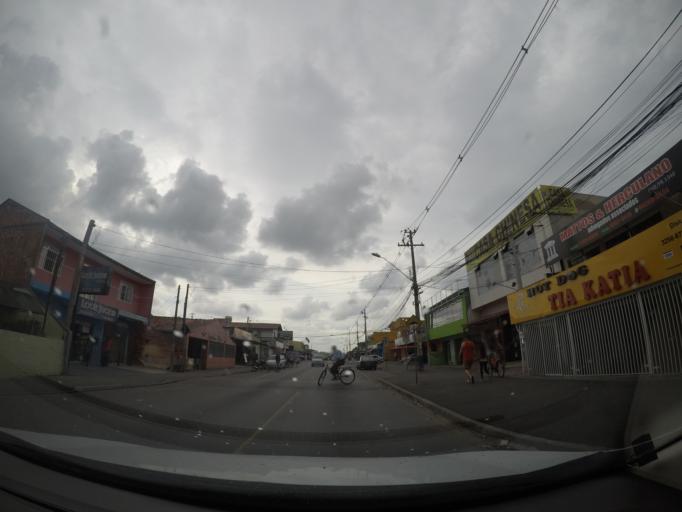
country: BR
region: Parana
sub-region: Sao Jose Dos Pinhais
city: Sao Jose dos Pinhais
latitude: -25.5510
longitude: -49.2486
